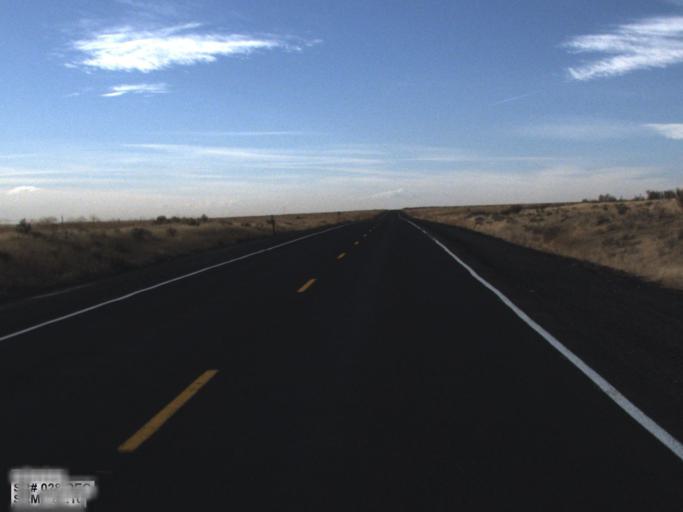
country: US
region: Washington
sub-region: Grant County
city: Warden
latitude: 47.3454
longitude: -118.9213
